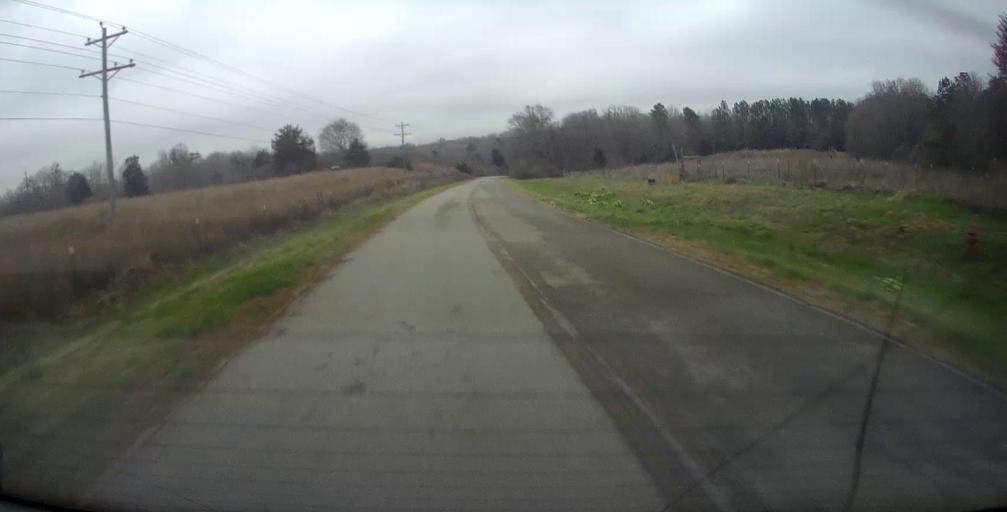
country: US
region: Georgia
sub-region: Lamar County
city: Barnesville
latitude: 33.0399
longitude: -84.1122
